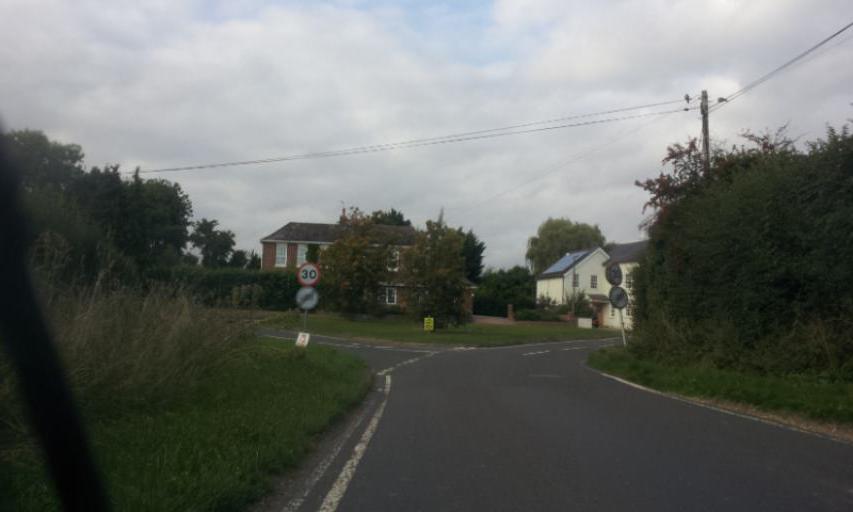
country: GB
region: England
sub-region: Kent
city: Hadlow
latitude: 51.2097
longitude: 0.3413
